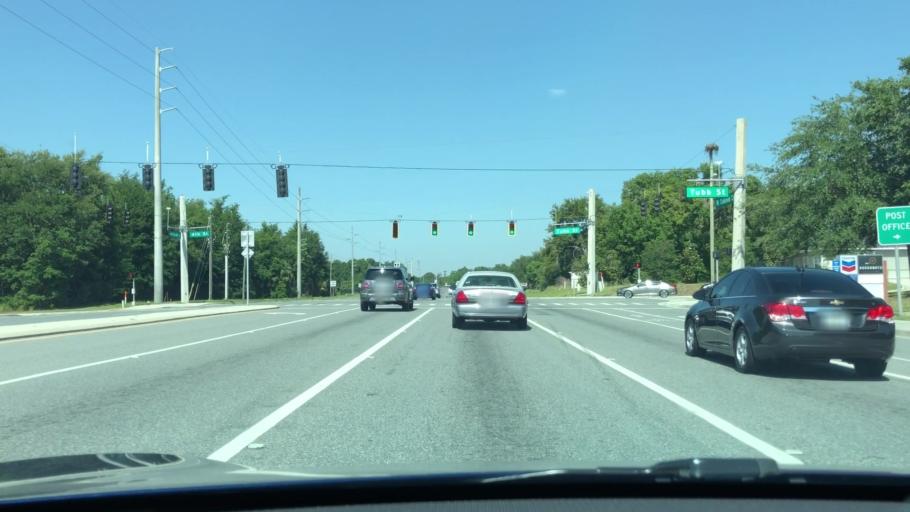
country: US
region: Florida
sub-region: Orange County
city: Oakland
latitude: 28.5512
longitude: -81.6275
